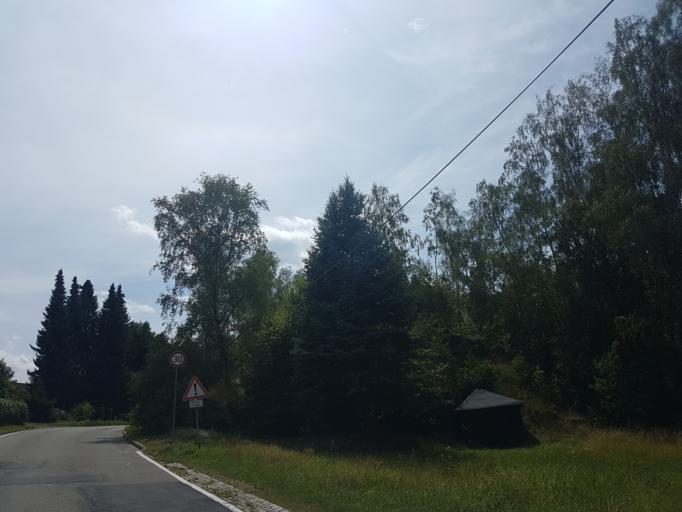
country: DE
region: Saxony
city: Freiberg
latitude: 50.8872
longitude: 13.3568
